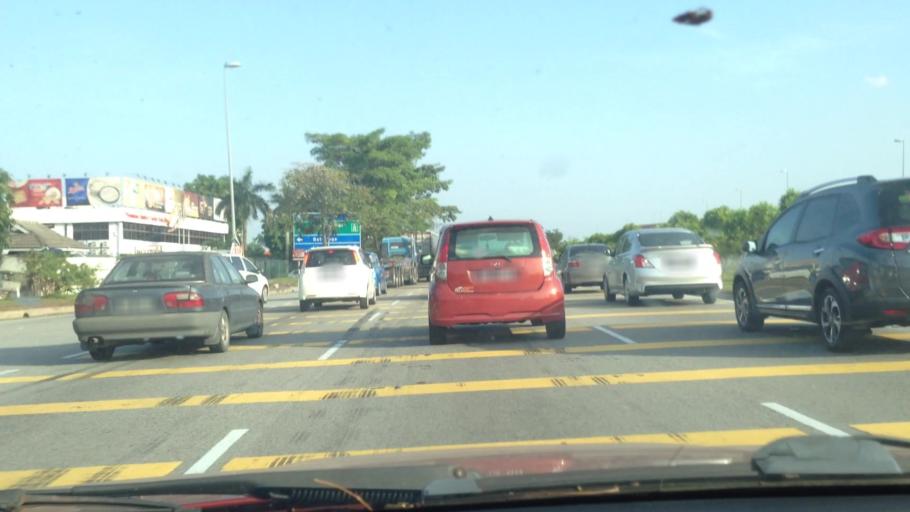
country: MY
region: Selangor
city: Subang Jaya
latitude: 3.0420
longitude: 101.5467
